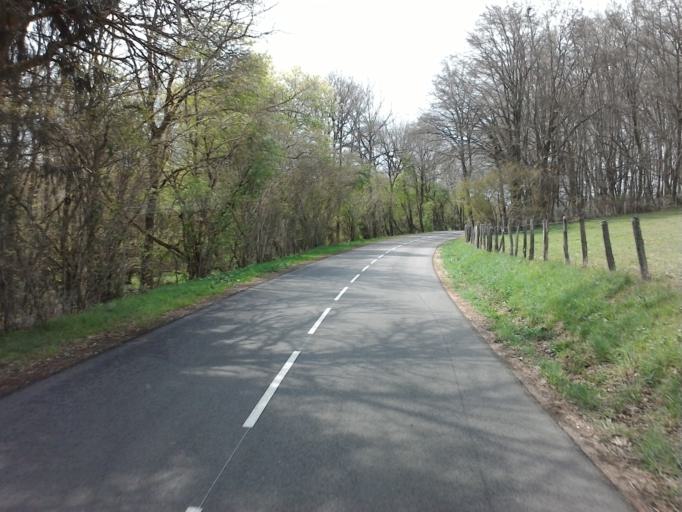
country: FR
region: Bourgogne
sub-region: Departement de la Cote-d'Or
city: Saulieu
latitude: 47.1789
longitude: 4.1046
